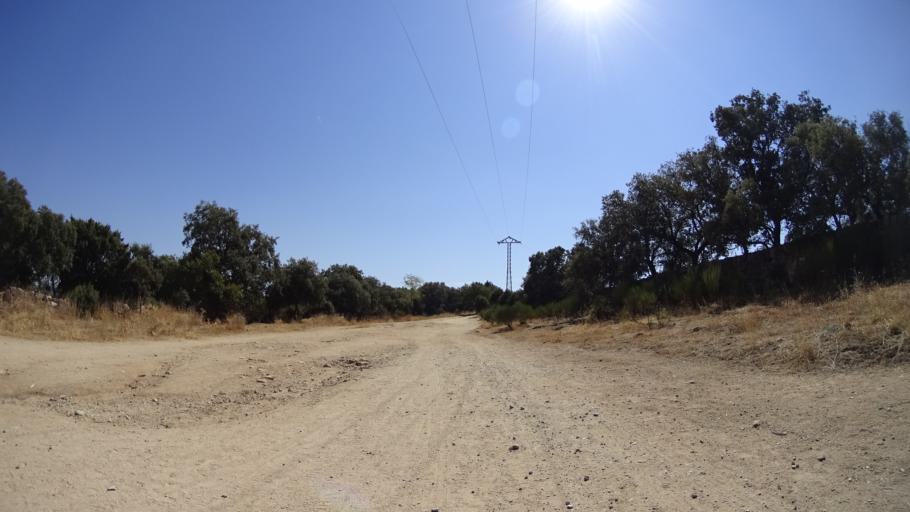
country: ES
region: Madrid
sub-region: Provincia de Madrid
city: Collado-Villalba
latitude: 40.6089
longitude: -4.0114
